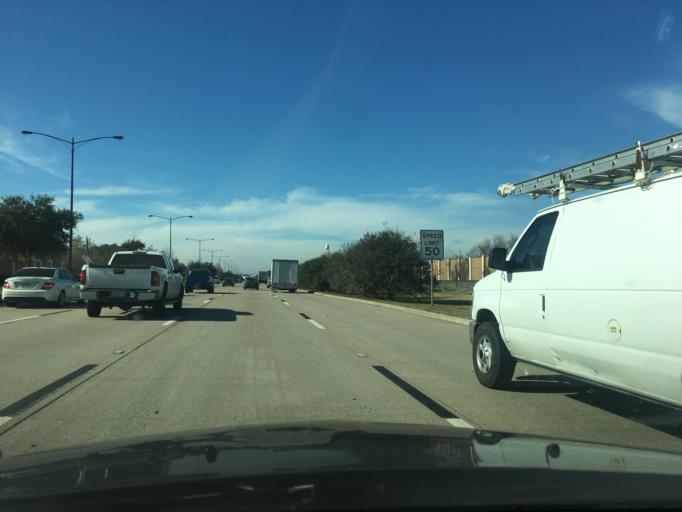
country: US
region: Texas
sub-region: Fort Bend County
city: Sugar Land
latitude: 29.6229
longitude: -95.6209
